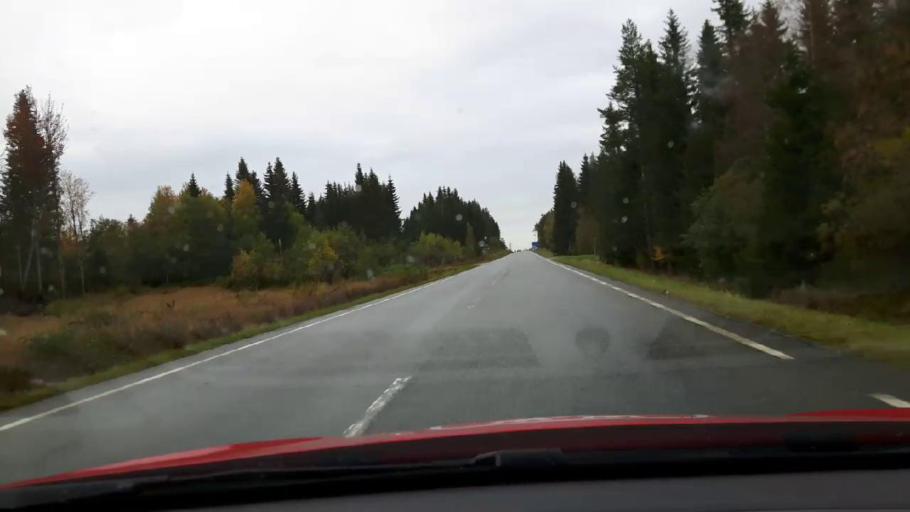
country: SE
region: Jaemtland
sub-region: Bergs Kommun
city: Hoverberg
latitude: 62.9089
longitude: 14.3309
